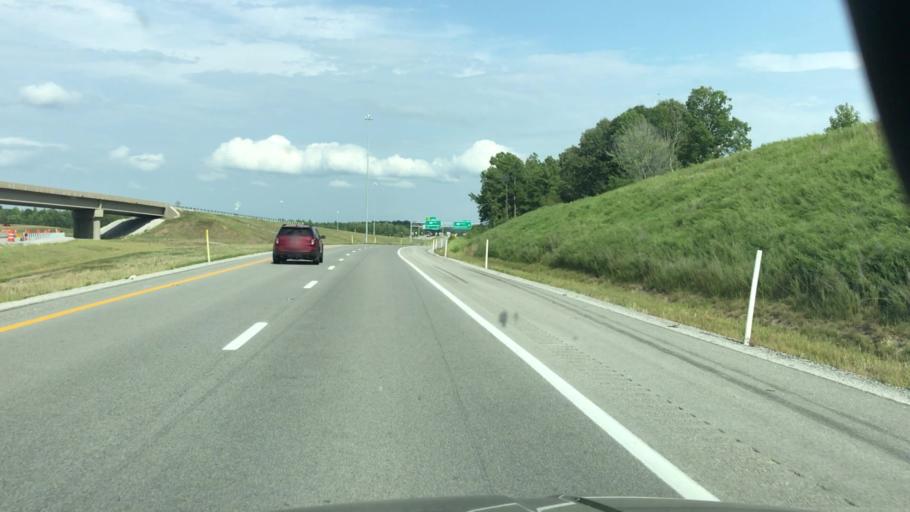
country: US
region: Kentucky
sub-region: Hopkins County
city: Nortonville
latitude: 37.2123
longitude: -87.4501
